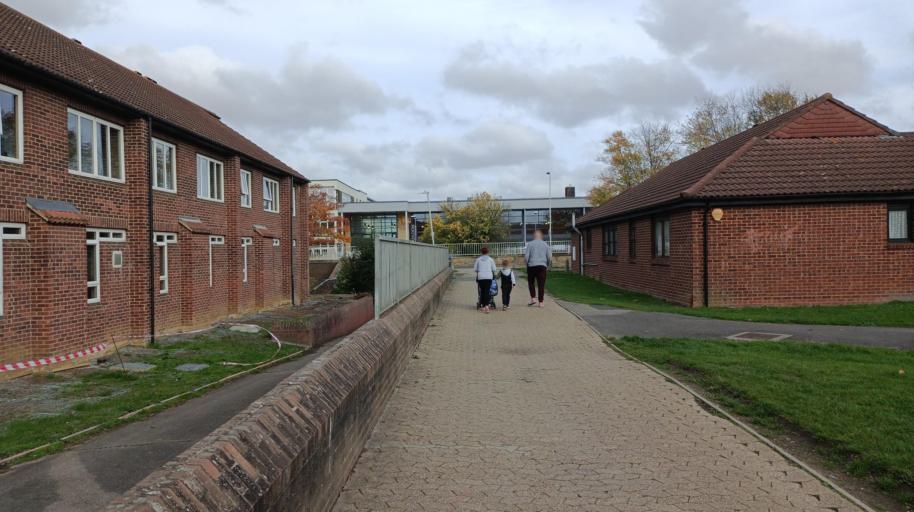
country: GB
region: England
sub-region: Essex
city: Pitsea
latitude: 51.5674
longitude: 0.5050
